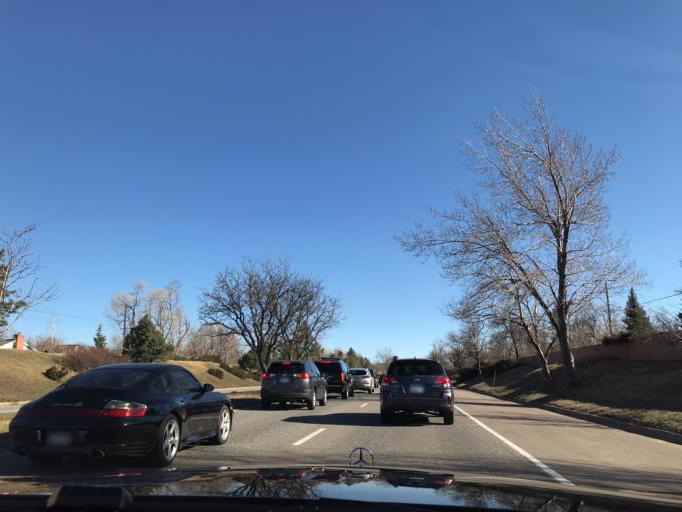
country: US
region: Colorado
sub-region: Boulder County
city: Boulder
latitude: 40.0050
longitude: -105.2369
